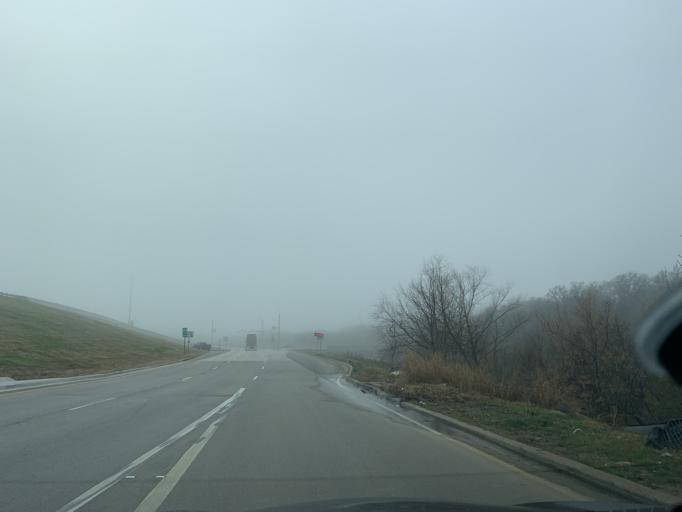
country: US
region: Texas
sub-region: Tarrant County
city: Euless
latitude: 32.8237
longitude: -97.0619
